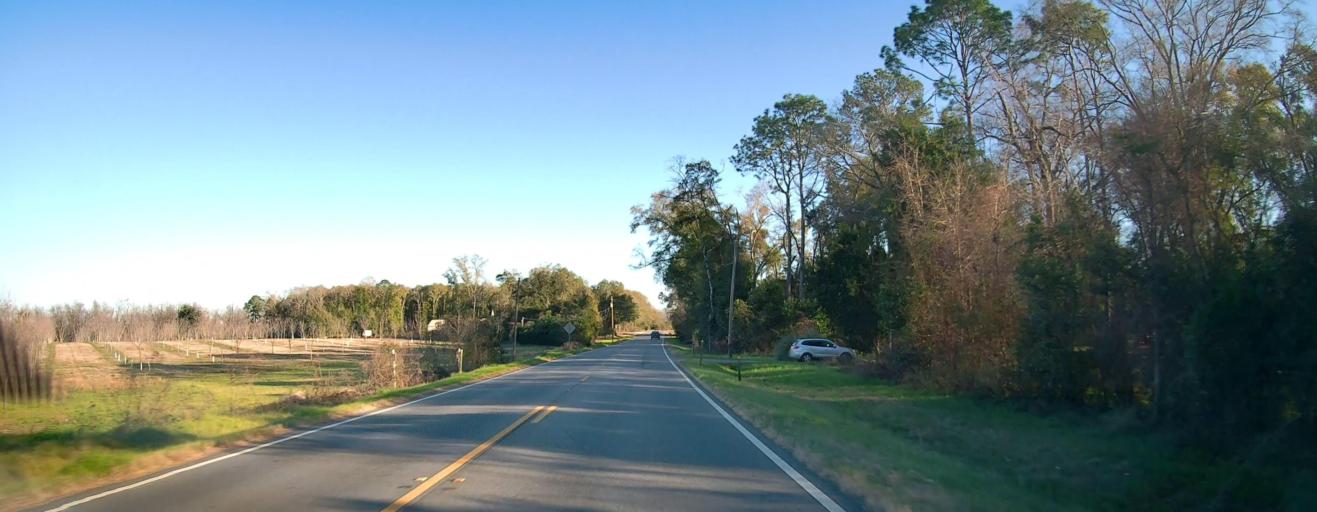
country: US
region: Georgia
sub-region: Dougherty County
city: Albany
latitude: 31.6403
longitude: -84.1677
